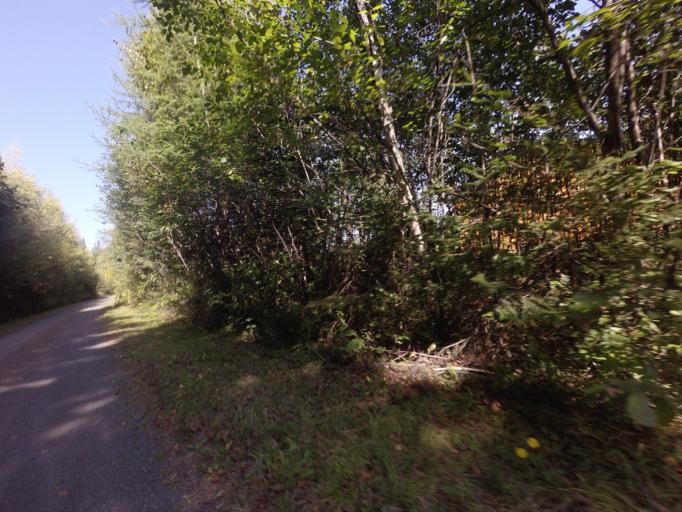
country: CA
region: Quebec
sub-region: Laurentides
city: Sainte-Agathe-des-Monts
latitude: 46.0683
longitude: -74.3137
